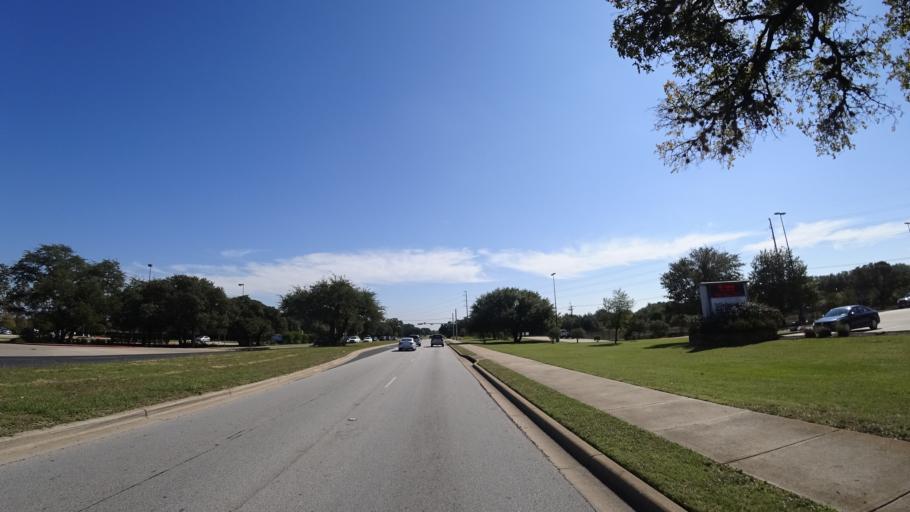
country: US
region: Texas
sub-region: Travis County
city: Shady Hollow
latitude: 30.1996
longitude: -97.8638
